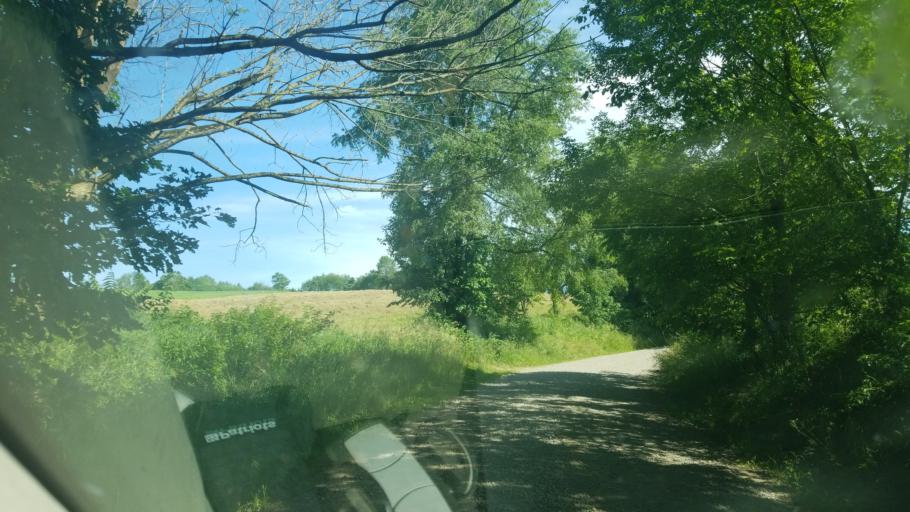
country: US
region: Ohio
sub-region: Holmes County
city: Millersburg
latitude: 40.4581
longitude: -81.9560
